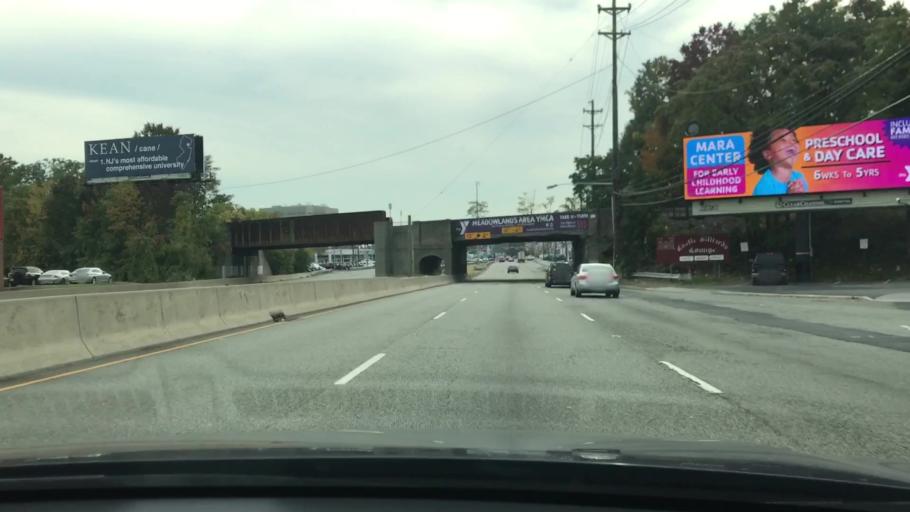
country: US
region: New Jersey
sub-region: Bergen County
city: Rutherford
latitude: 40.8241
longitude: -74.0978
